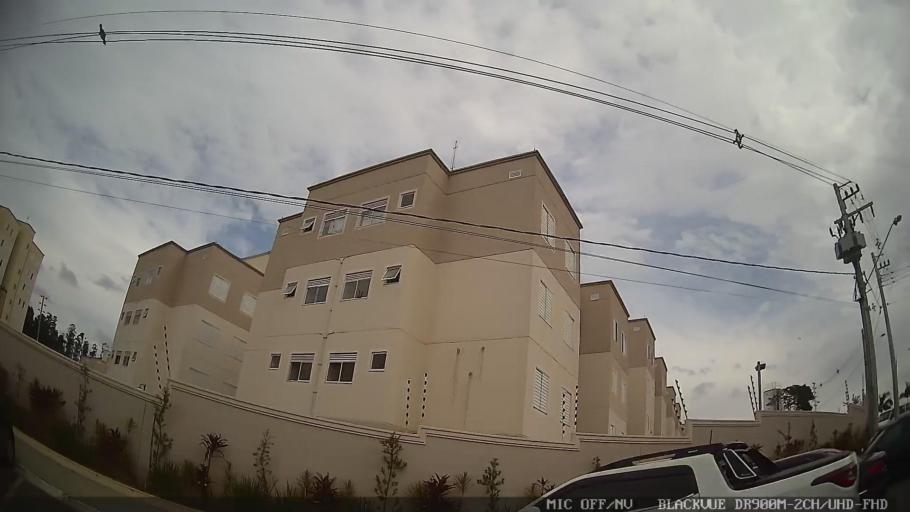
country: BR
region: Sao Paulo
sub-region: Salto
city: Salto
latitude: -23.1991
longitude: -47.2718
